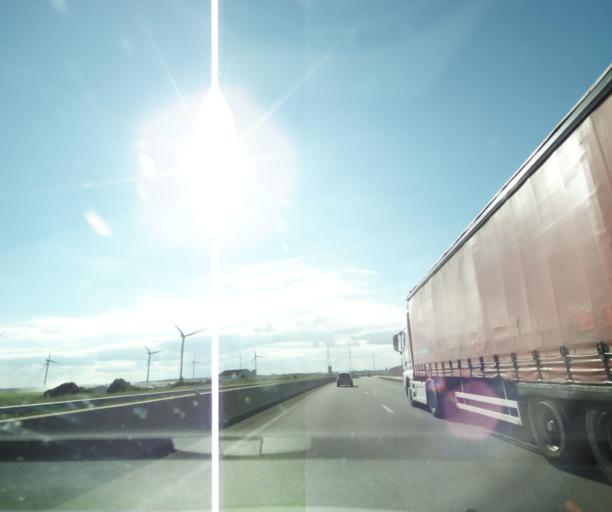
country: FR
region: Centre
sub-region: Departement d'Eure-et-Loir
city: Voves
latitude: 48.3267
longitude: 1.6568
